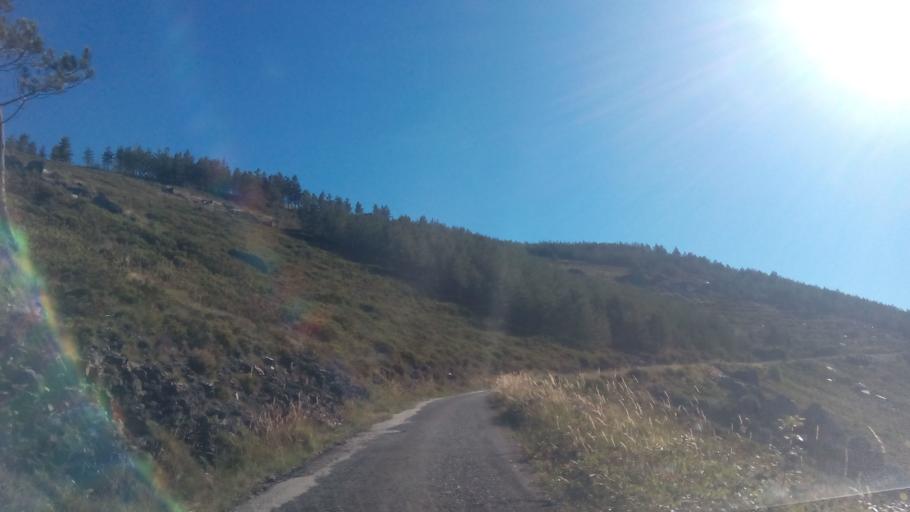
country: PT
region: Vila Real
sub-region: Mesao Frio
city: Mesao Frio
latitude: 41.2678
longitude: -7.9216
